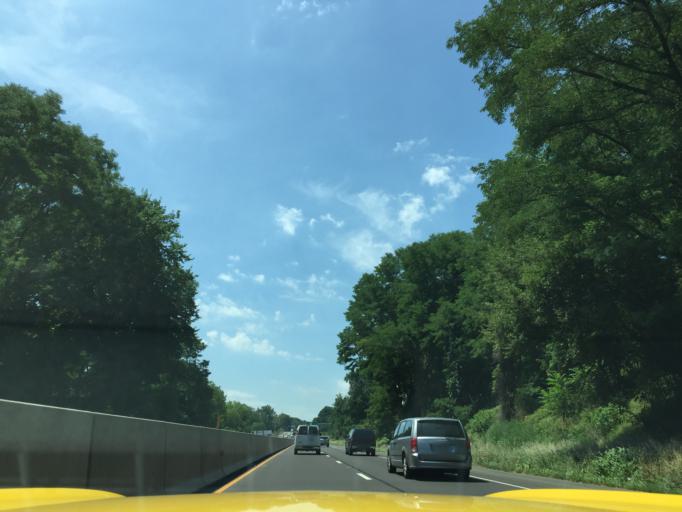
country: US
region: Pennsylvania
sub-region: Bucks County
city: Woodbourne
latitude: 40.1832
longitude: -74.9018
